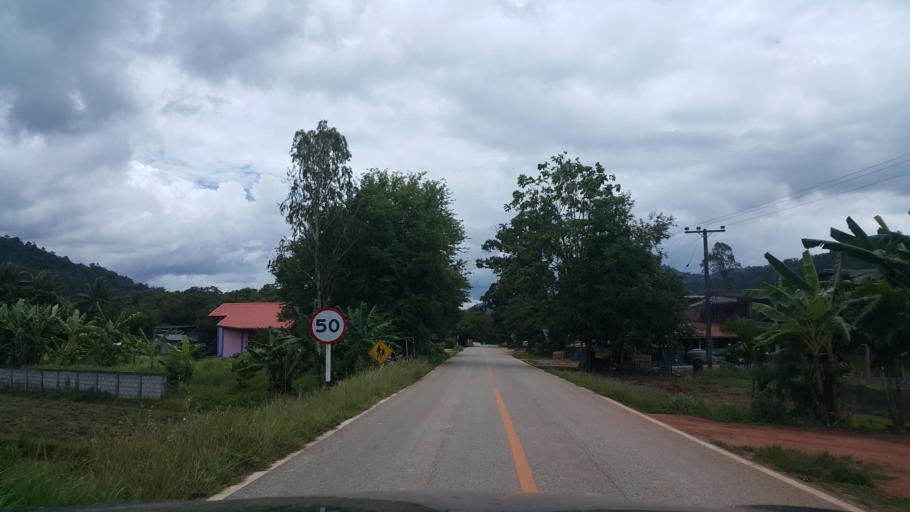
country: TH
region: Phitsanulok
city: Chat Trakan
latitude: 17.3840
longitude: 100.7544
